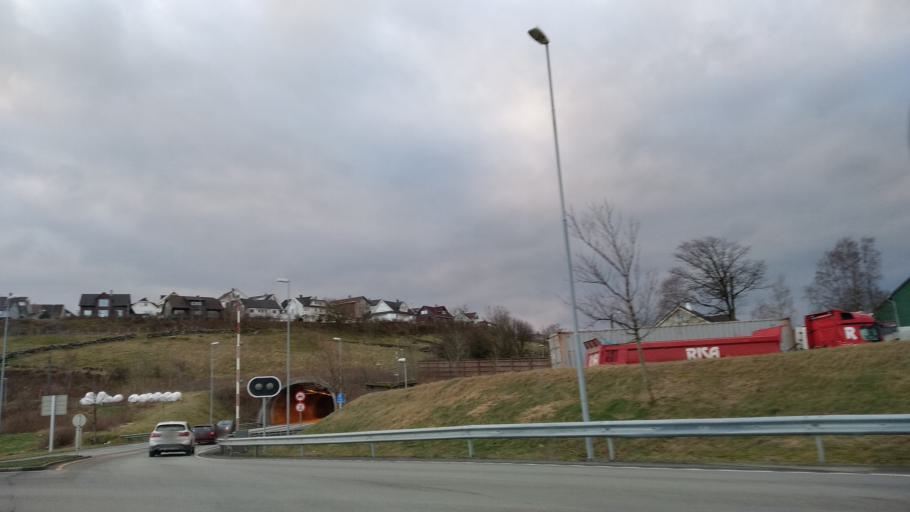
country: NO
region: Rogaland
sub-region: Klepp
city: Kleppe
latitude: 58.7789
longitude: 5.6234
